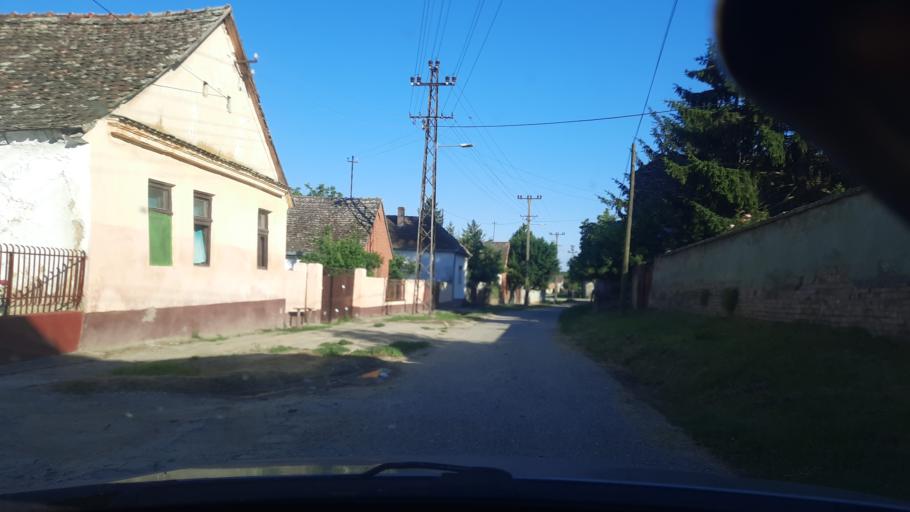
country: RS
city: Cortanovci
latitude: 45.1143
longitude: 19.9443
